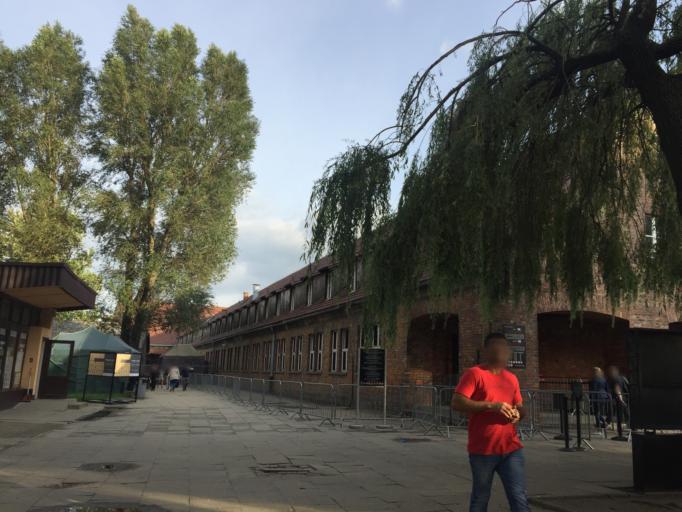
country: PL
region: Lesser Poland Voivodeship
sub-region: Powiat oswiecimski
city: Oswiecim
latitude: 50.0279
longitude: 19.2017
